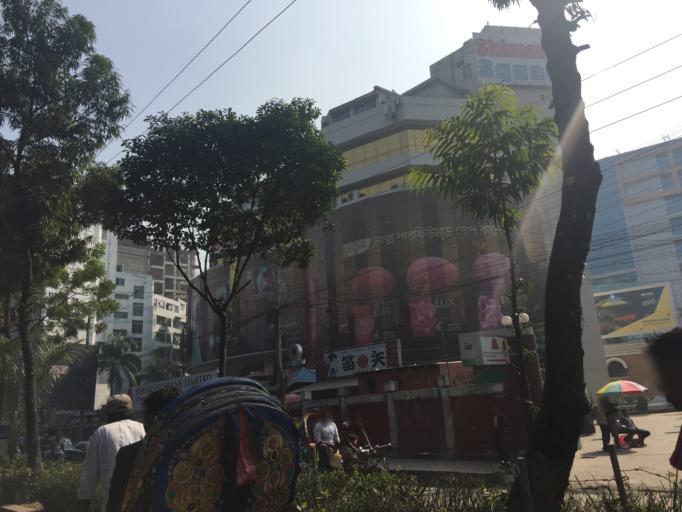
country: BD
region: Dhaka
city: Azimpur
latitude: 23.7384
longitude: 90.3765
